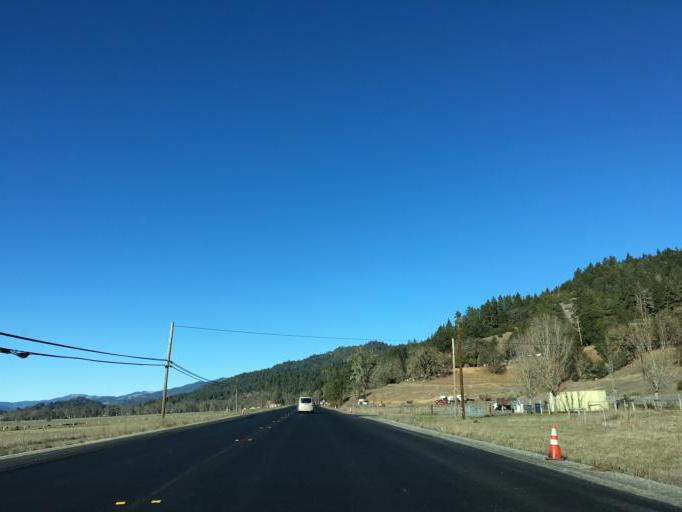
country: US
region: California
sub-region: Mendocino County
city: Laytonville
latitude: 39.6680
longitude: -123.4761
